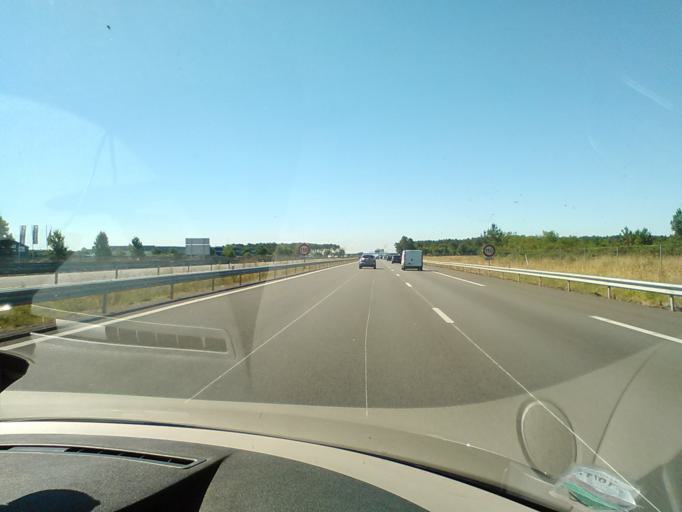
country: FR
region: Aquitaine
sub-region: Departement des Landes
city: Saint-Geours-de-Maremne
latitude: 43.7206
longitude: -1.2276
